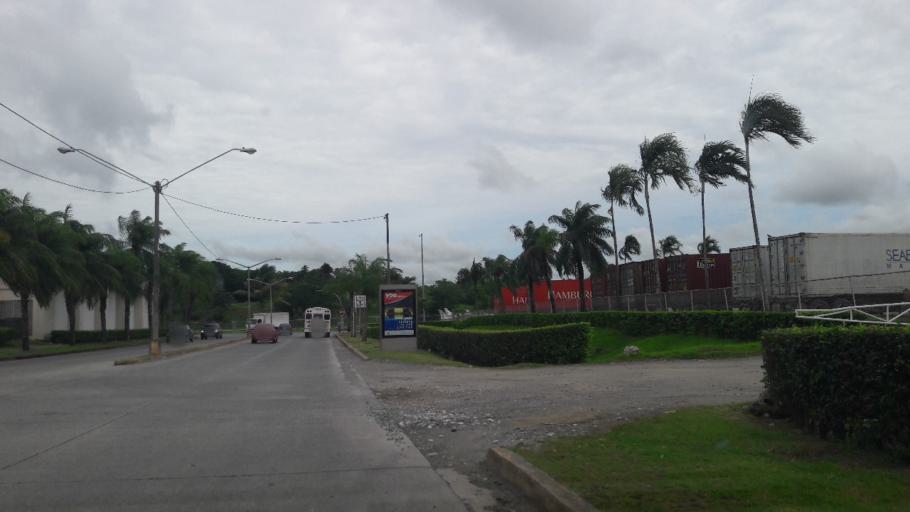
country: PA
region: Panama
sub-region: Distrito de Panama
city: Ancon
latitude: 8.9783
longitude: -79.5525
